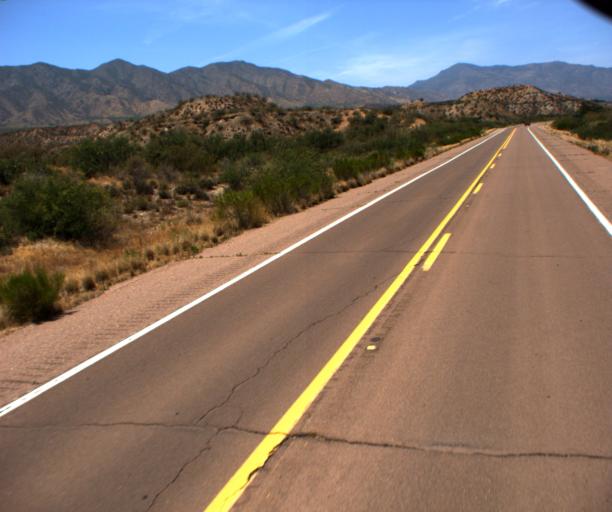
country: US
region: Arizona
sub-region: Gila County
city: Tonto Basin
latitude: 33.8201
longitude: -111.2903
